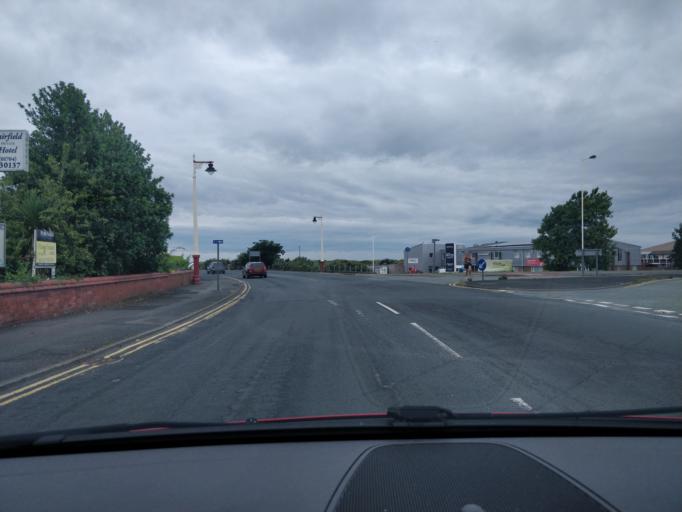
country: GB
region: England
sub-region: Sefton
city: Southport
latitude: 53.6591
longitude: -2.9971
